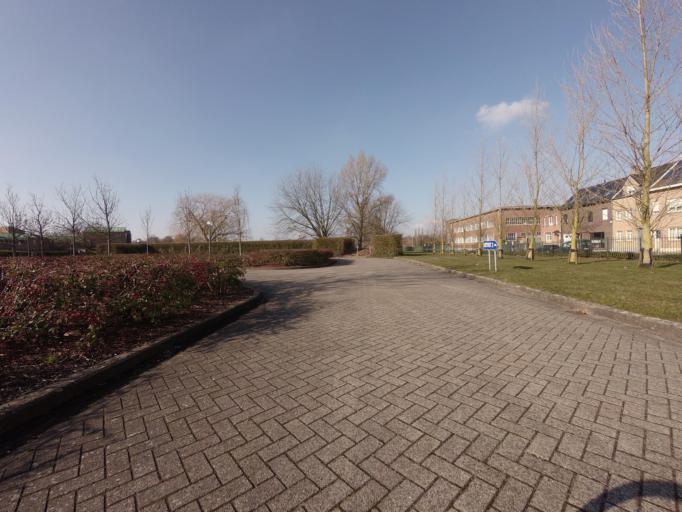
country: BE
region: Flanders
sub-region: Provincie Antwerpen
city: Hoboken
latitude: 51.1695
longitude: 4.3757
